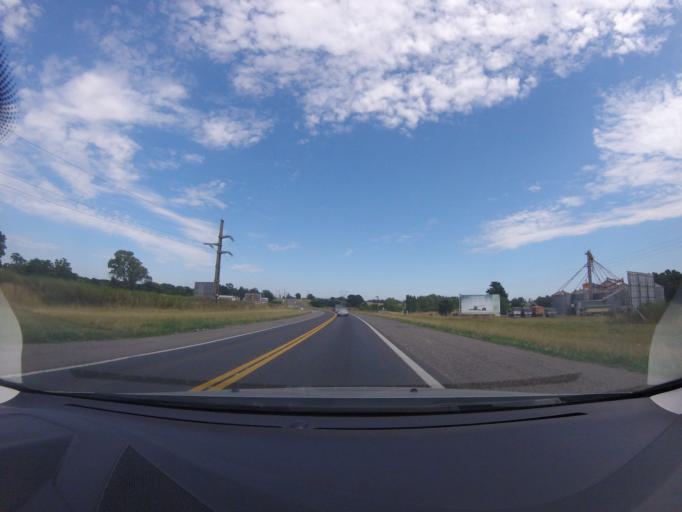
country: AR
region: Buenos Aires
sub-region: Partido de Tandil
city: Tandil
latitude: -37.2896
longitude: -59.1485
